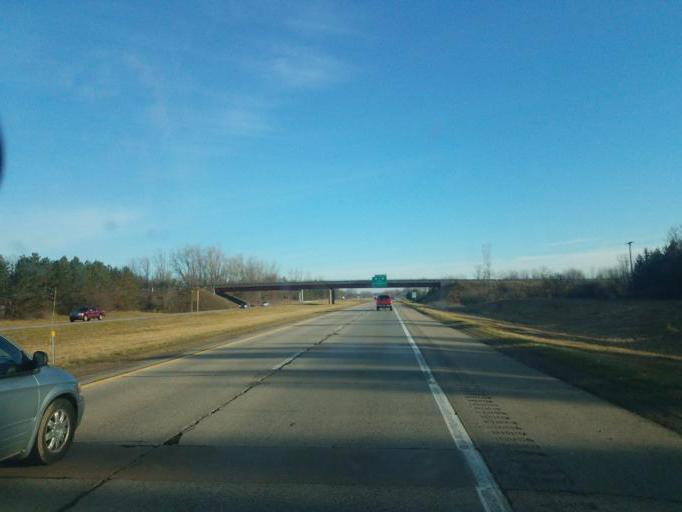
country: US
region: Michigan
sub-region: Ingham County
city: East Lansing
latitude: 42.7821
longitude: -84.5136
